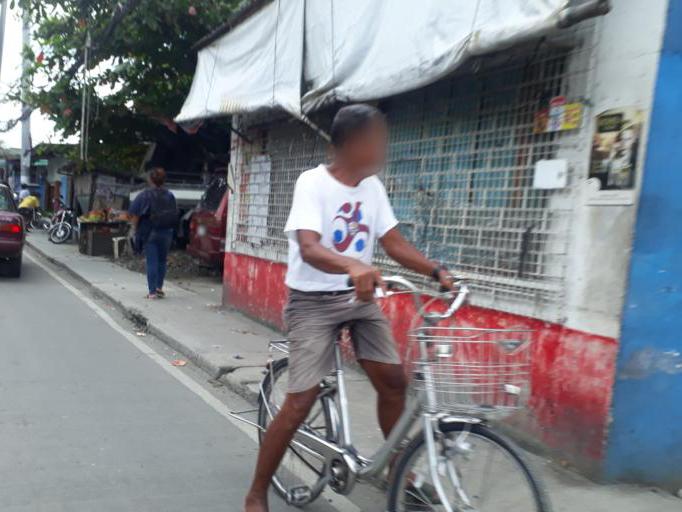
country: PH
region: Calabarzon
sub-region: Province of Rizal
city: Valenzuela
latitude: 14.6995
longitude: 120.9577
